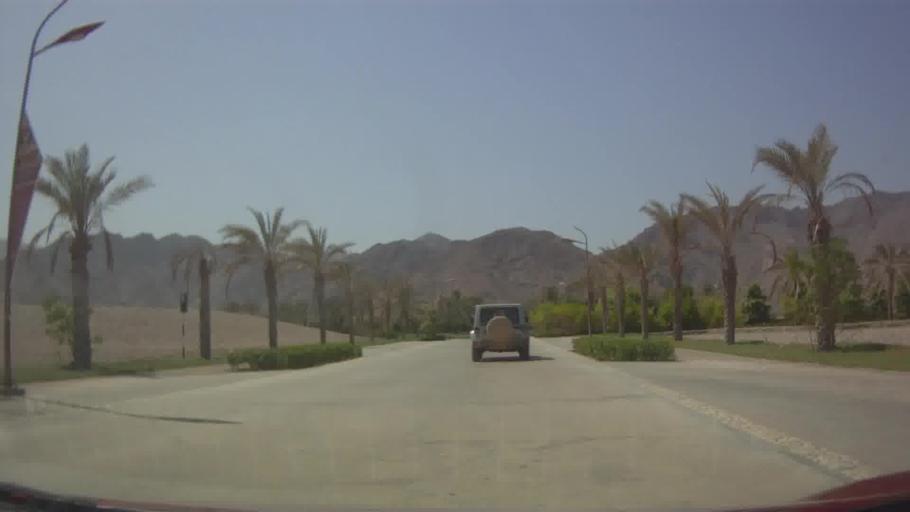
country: OM
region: Muhafazat Masqat
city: Muscat
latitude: 23.4132
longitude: 58.7885
